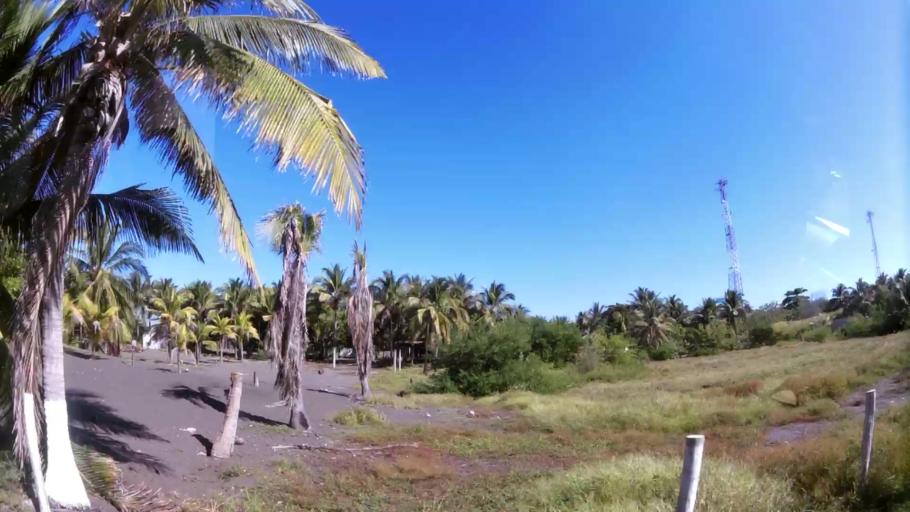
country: GT
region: Santa Rosa
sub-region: Municipio de Taxisco
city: Taxisco
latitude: 13.8668
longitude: -90.4152
